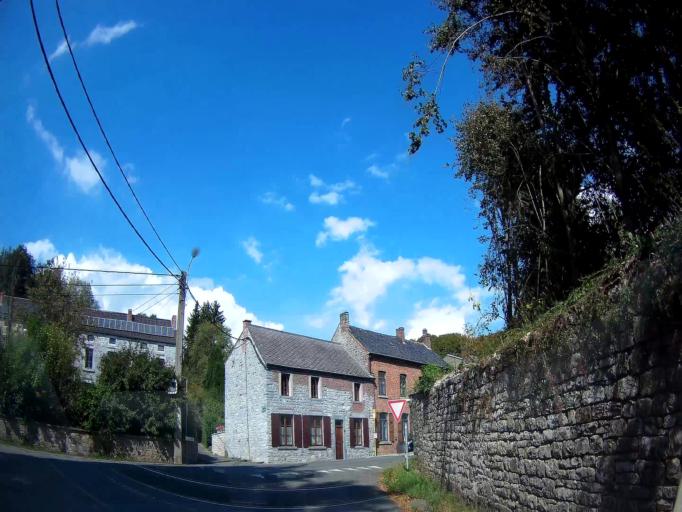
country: BE
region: Wallonia
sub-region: Province de Namur
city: Profondeville
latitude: 50.3444
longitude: 4.8412
